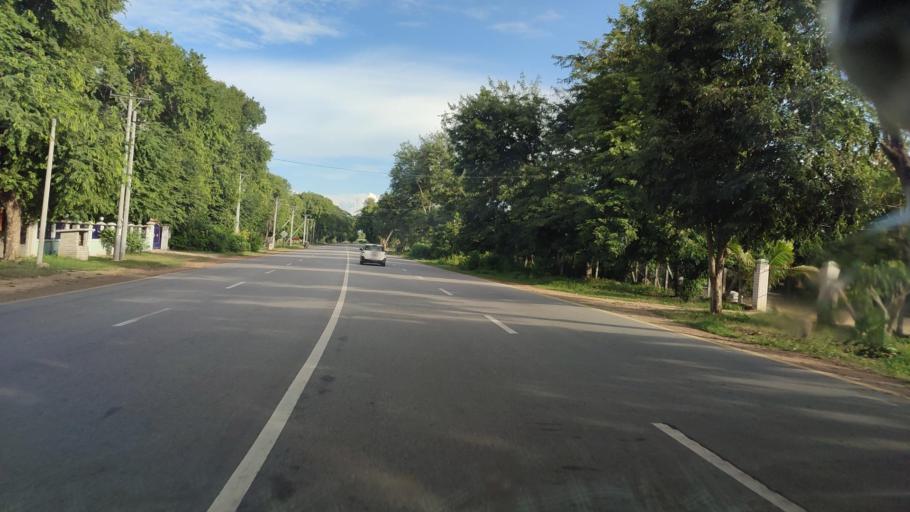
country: MM
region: Mandalay
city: Yamethin
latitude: 20.1867
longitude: 96.1862
